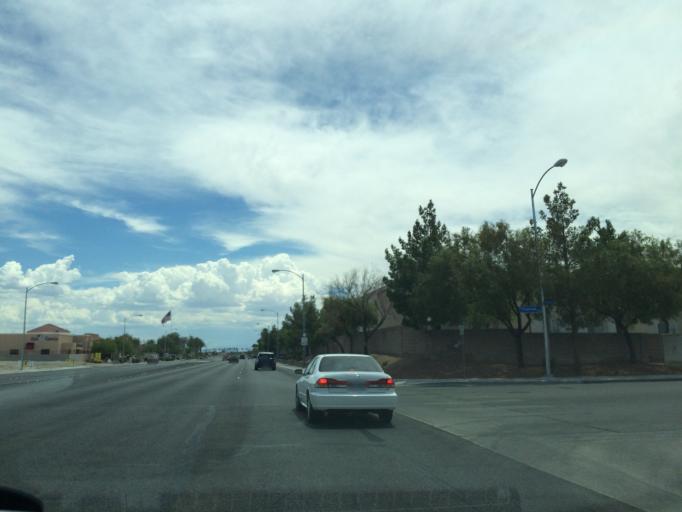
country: US
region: Nevada
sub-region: Clark County
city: North Las Vegas
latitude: 36.2655
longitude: -115.1801
